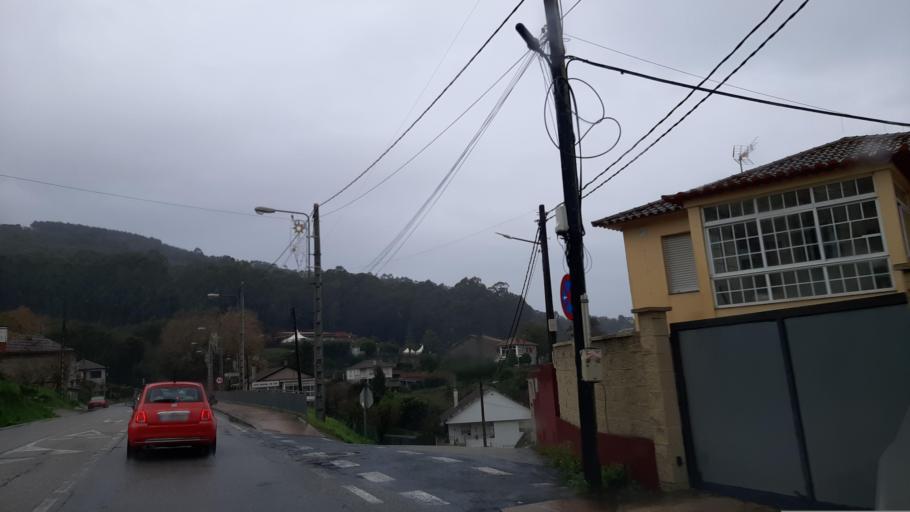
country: ES
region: Galicia
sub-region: Provincia de Pontevedra
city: Nigran
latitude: 42.1850
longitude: -8.7876
